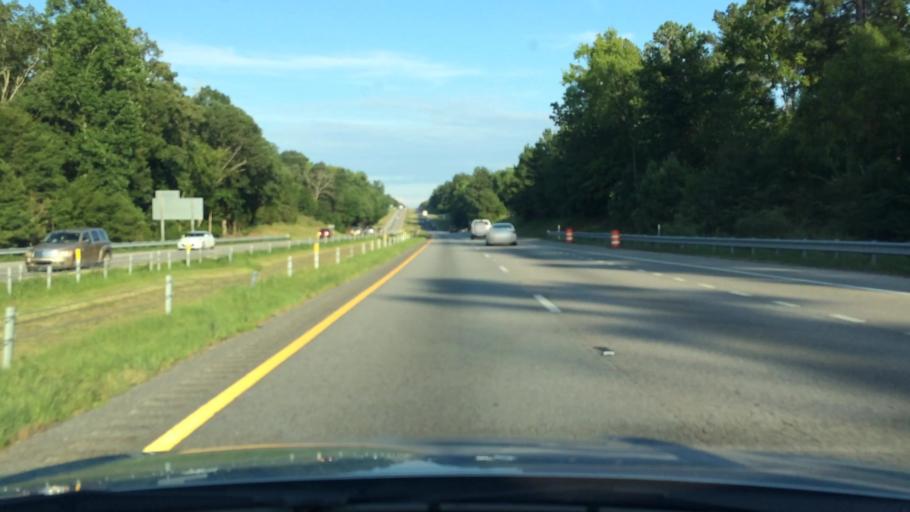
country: US
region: South Carolina
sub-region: Newberry County
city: Newberry
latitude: 34.2900
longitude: -81.5412
